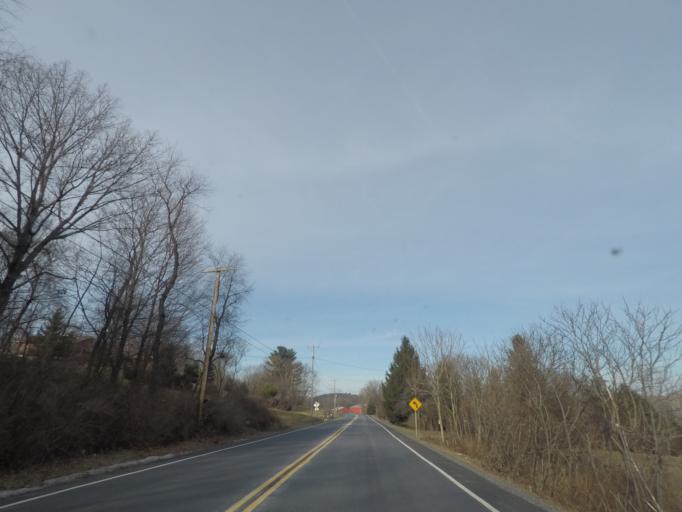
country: US
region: New York
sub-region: Columbia County
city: Valatie
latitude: 42.3886
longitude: -73.6432
